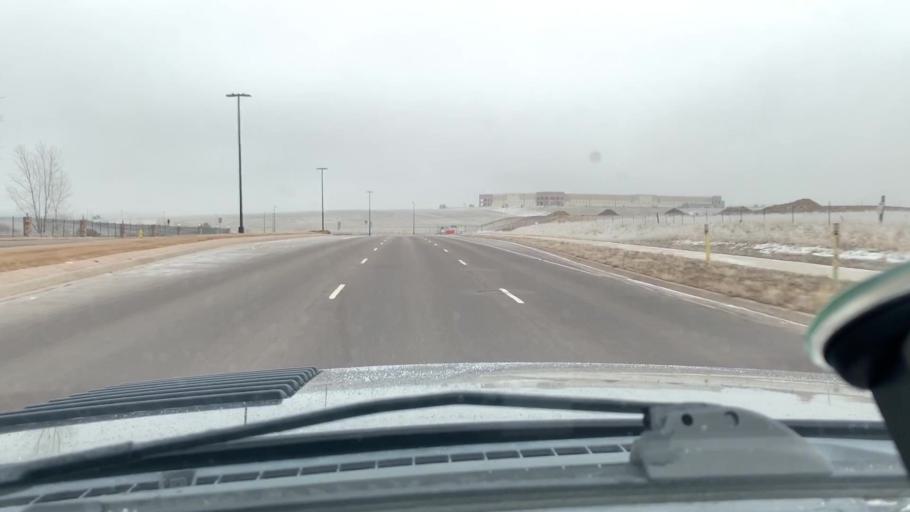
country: US
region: Colorado
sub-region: Arapahoe County
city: Dove Valley
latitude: 39.5775
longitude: -104.8215
